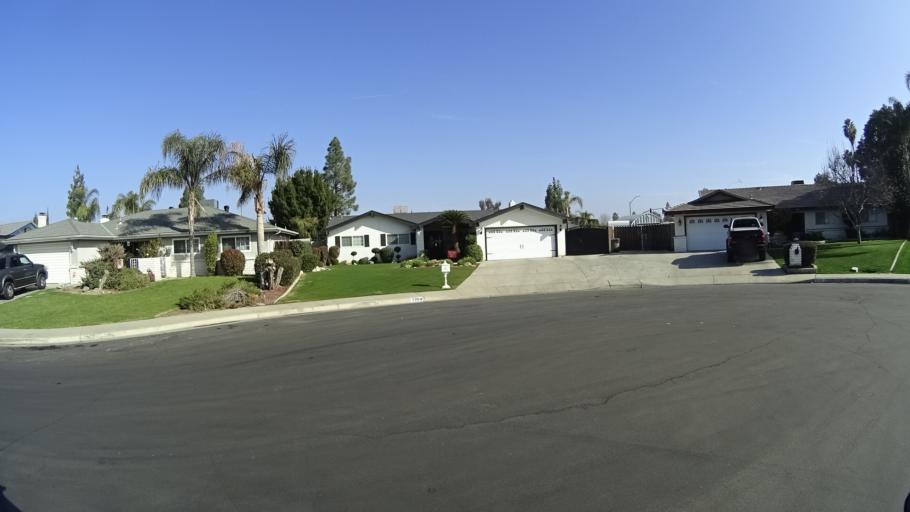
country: US
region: California
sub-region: Kern County
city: Bakersfield
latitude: 35.3326
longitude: -119.0592
